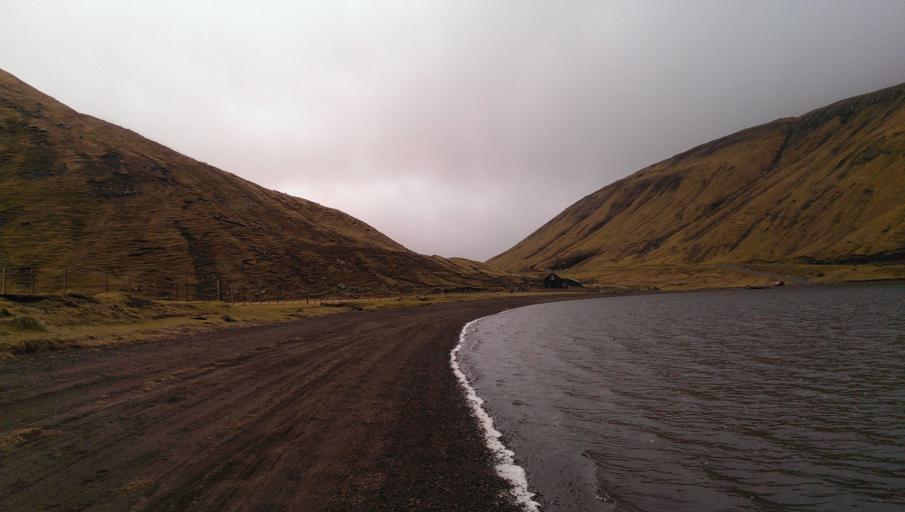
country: FO
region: Streymoy
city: Kollafjordhur
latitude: 62.1310
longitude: -7.0205
